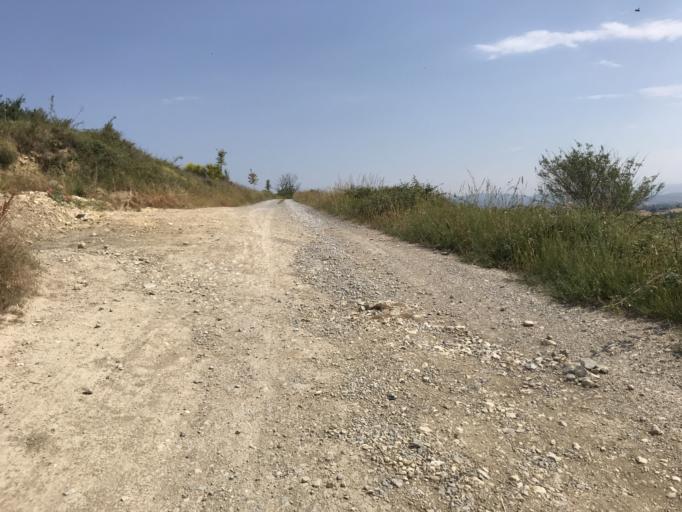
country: ES
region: Basque Country
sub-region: Provincia de Alava
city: Gasteiz / Vitoria
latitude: 42.8310
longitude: -2.6495
